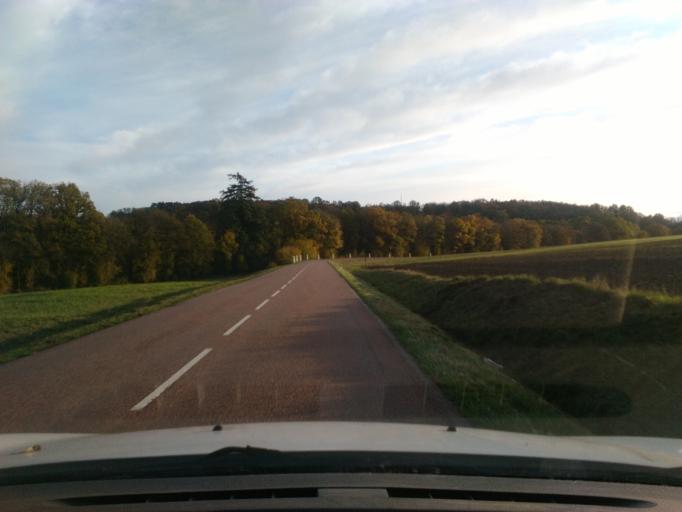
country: FR
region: Lorraine
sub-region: Departement des Vosges
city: Mirecourt
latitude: 48.2195
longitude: 6.1564
